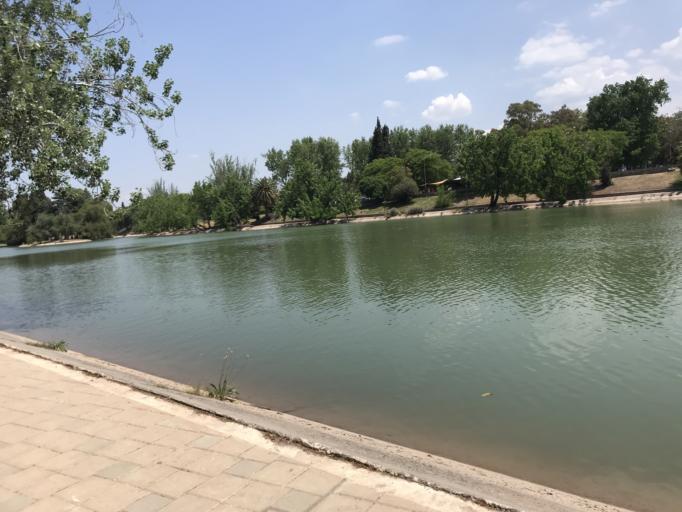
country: AR
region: Mendoza
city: Mendoza
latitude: -32.8943
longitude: -68.8650
